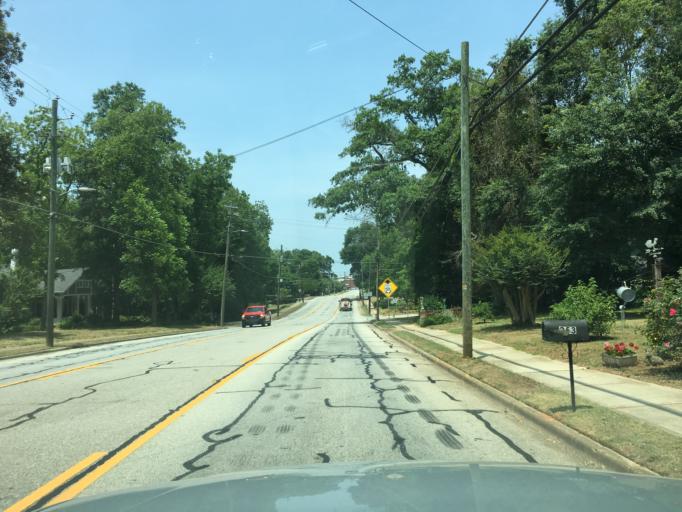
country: US
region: Georgia
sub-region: Hart County
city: Hartwell
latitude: 34.3485
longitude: -82.9291
